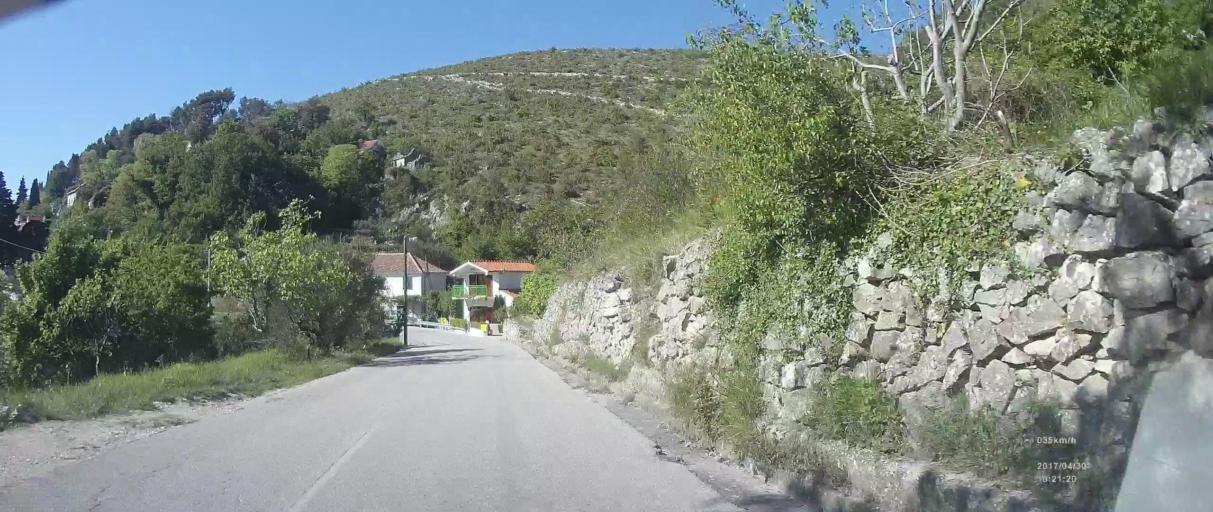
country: HR
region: Splitsko-Dalmatinska
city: Srinjine
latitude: 43.5050
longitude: 16.5989
